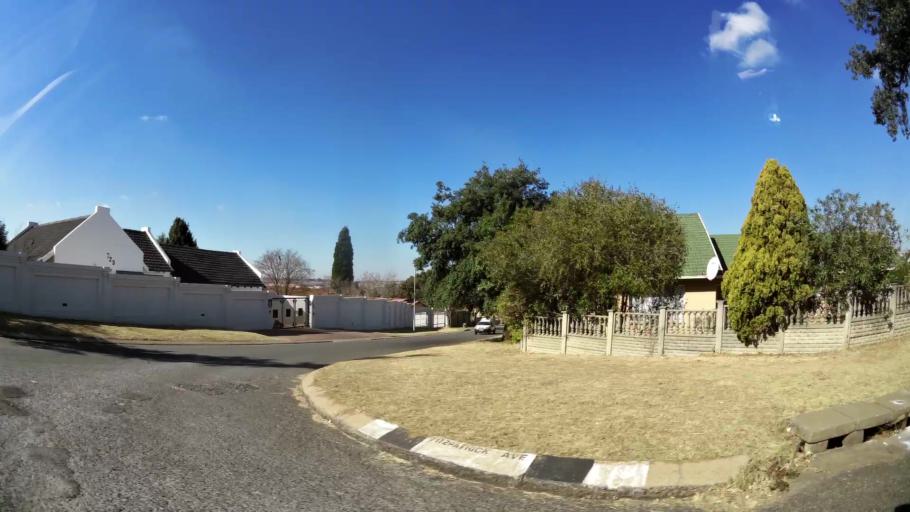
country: ZA
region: Gauteng
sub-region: City of Johannesburg Metropolitan Municipality
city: Roodepoort
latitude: -26.1480
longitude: 27.8369
